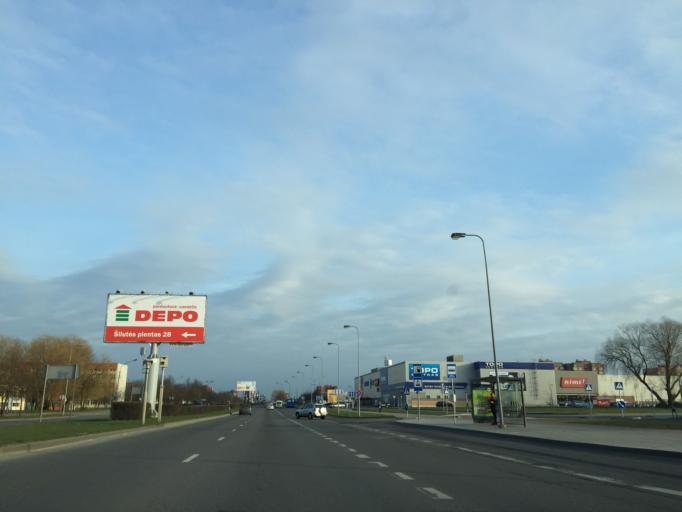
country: LT
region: Klaipedos apskritis
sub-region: Klaipeda
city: Klaipeda
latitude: 55.6893
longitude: 21.1557
